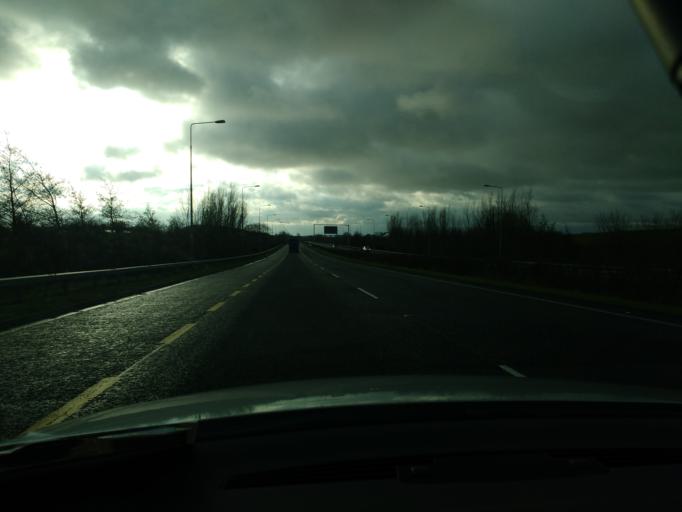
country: IE
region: Munster
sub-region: An Clar
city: Shannon
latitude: 52.7236
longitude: -8.8765
